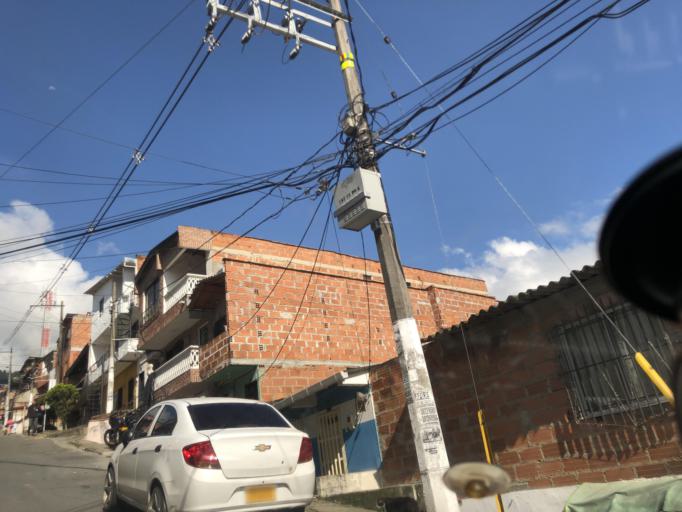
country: CO
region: Antioquia
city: Bello
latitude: 6.3135
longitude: -75.5759
